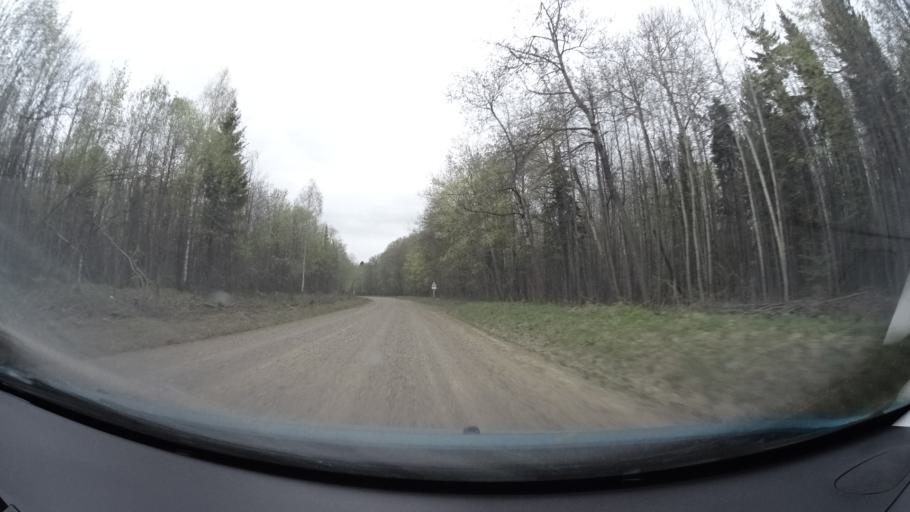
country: RU
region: Perm
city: Kuyeda
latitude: 56.5884
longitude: 55.7006
